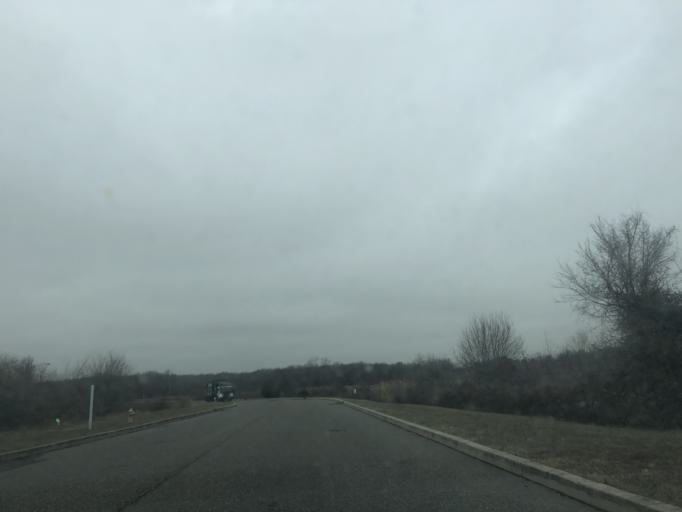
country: US
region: New Jersey
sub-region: Monmouth County
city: Allentown
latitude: 40.1861
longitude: -74.5882
